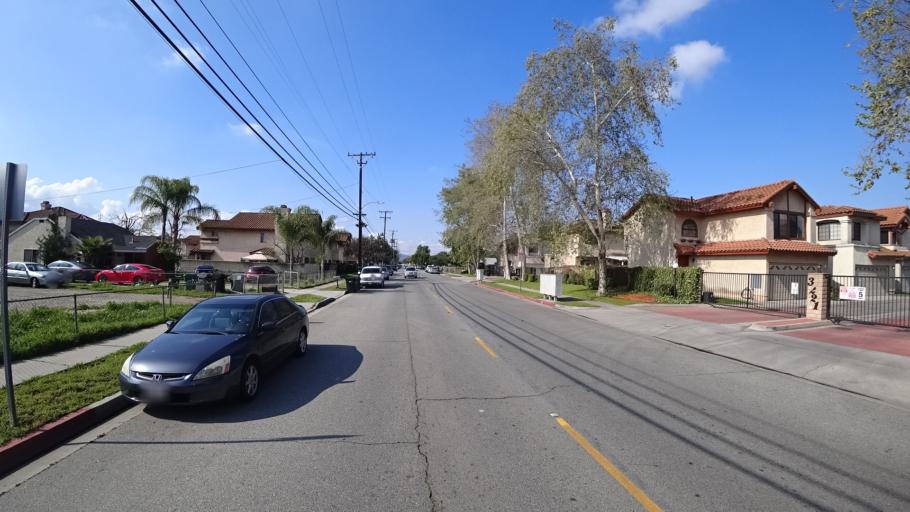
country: US
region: California
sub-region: Los Angeles County
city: Baldwin Park
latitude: 34.0729
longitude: -117.9677
